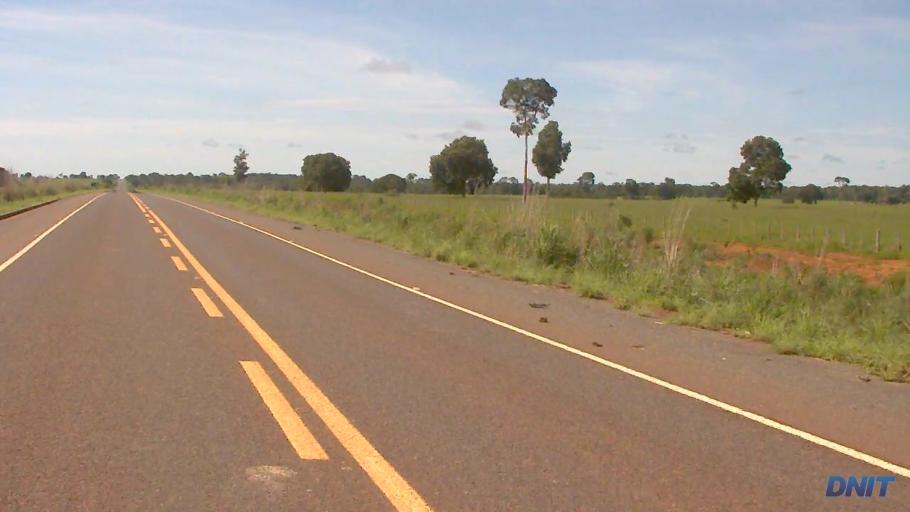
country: BR
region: Goias
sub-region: Sao Miguel Do Araguaia
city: Sao Miguel do Araguaia
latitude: -13.3831
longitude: -50.1401
